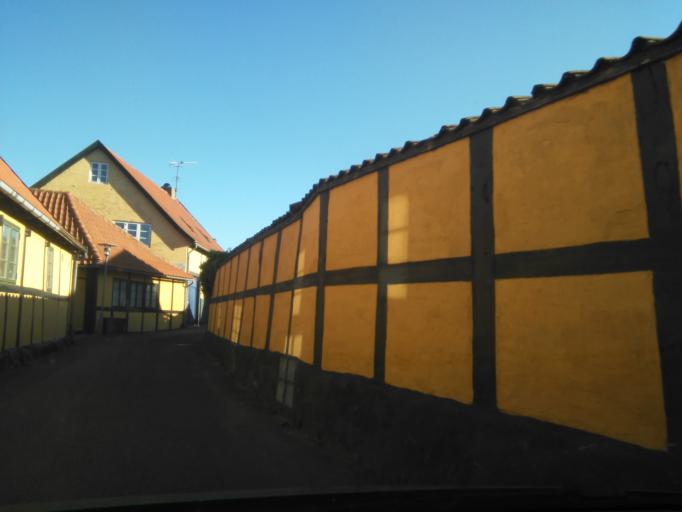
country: DK
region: Capital Region
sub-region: Bornholm Kommune
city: Ronne
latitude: 55.2757
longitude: 14.8044
